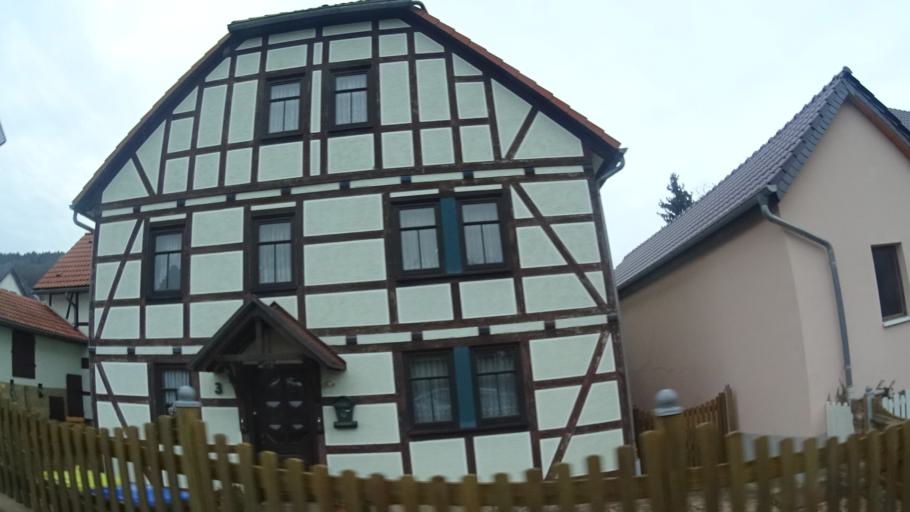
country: DE
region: Thuringia
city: Dorndorf
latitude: 50.8246
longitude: 10.1134
